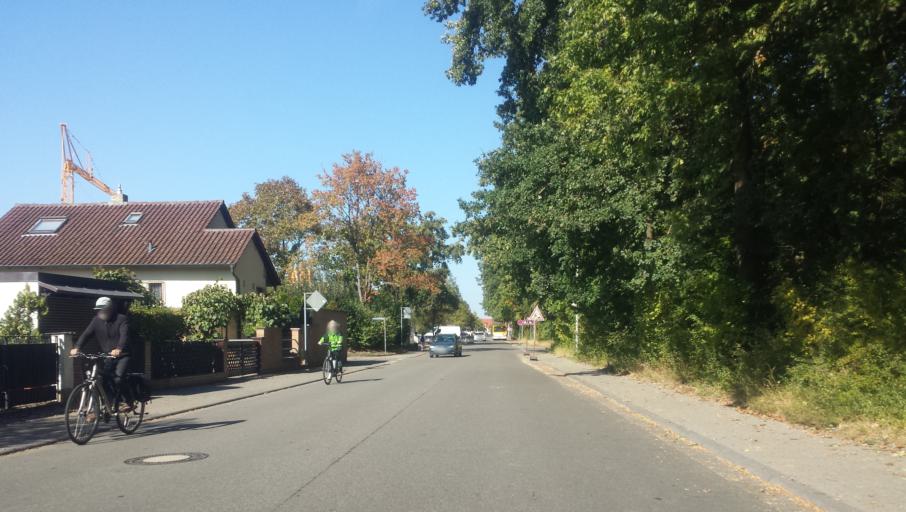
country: DE
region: Rheinland-Pfalz
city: Schifferstadt
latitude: 49.3804
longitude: 8.3952
